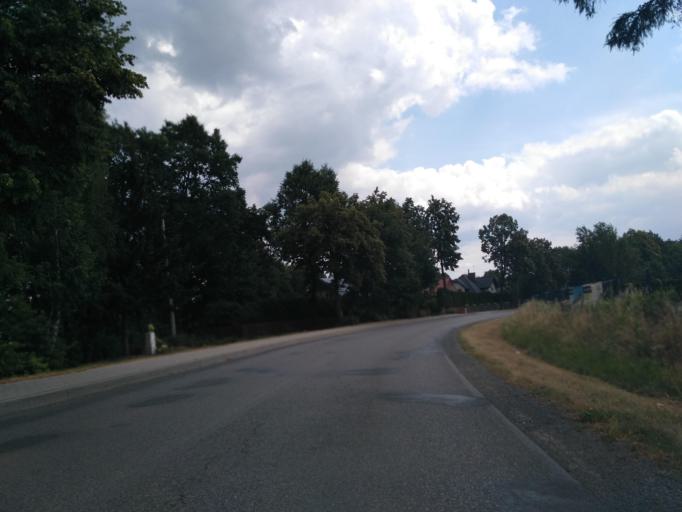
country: PL
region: Subcarpathian Voivodeship
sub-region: Powiat debicki
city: Zyrakow
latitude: 50.0608
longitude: 21.3510
